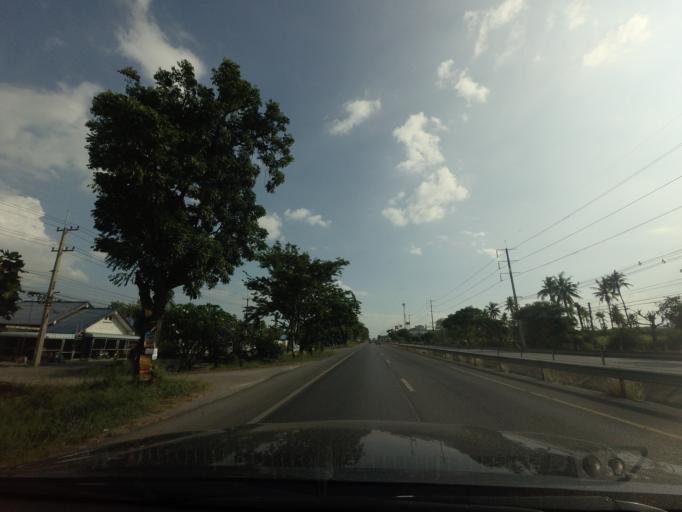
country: TH
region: Lop Buri
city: Phatthana Nikhom
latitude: 14.8221
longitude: 100.9111
